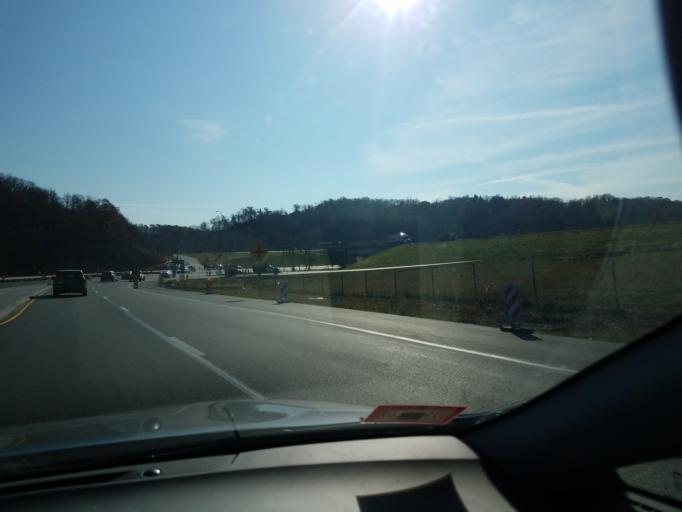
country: US
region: Pennsylvania
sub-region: Allegheny County
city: Ben Avon
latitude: 40.5270
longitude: -80.0706
